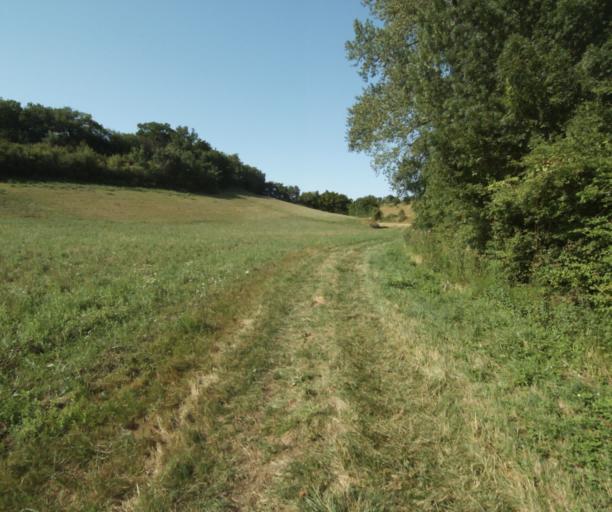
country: FR
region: Midi-Pyrenees
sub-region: Departement de la Haute-Garonne
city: Avignonet-Lauragais
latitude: 43.4205
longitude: 1.8249
